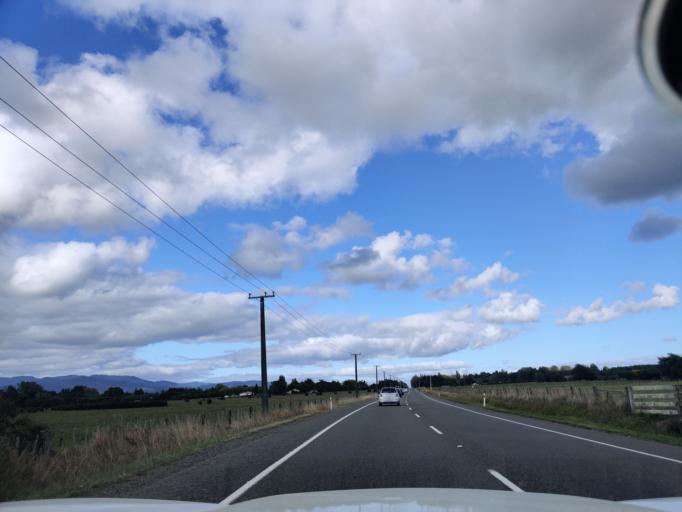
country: NZ
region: Manawatu-Wanganui
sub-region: Horowhenua District
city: Levin
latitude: -40.6080
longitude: 175.3294
